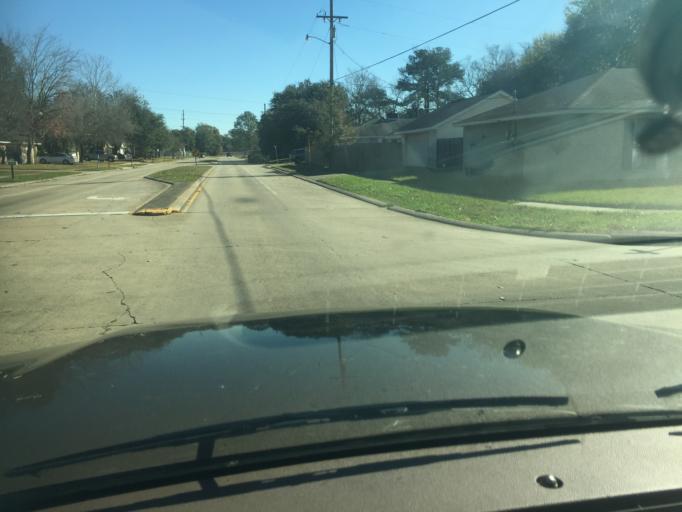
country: US
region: Louisiana
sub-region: Saint Tammany Parish
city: Slidell
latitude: 30.3017
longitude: -89.7708
